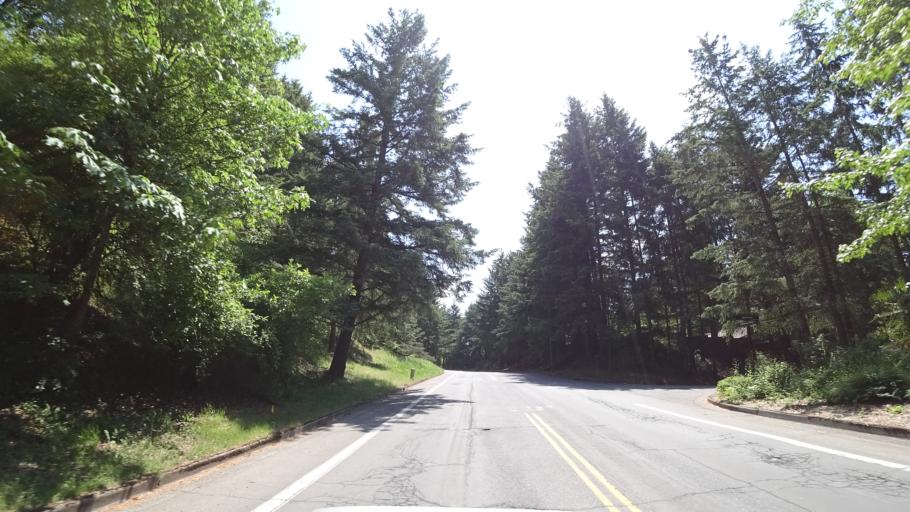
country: US
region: Oregon
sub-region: Washington County
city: Metzger
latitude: 45.4320
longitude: -122.7208
